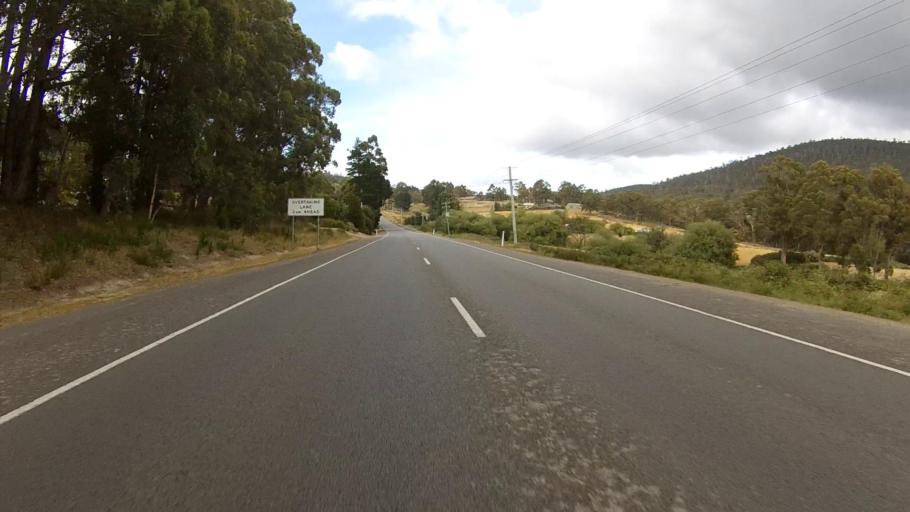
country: AU
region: Tasmania
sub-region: Kingborough
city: Kettering
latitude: -43.0837
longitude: 147.2531
